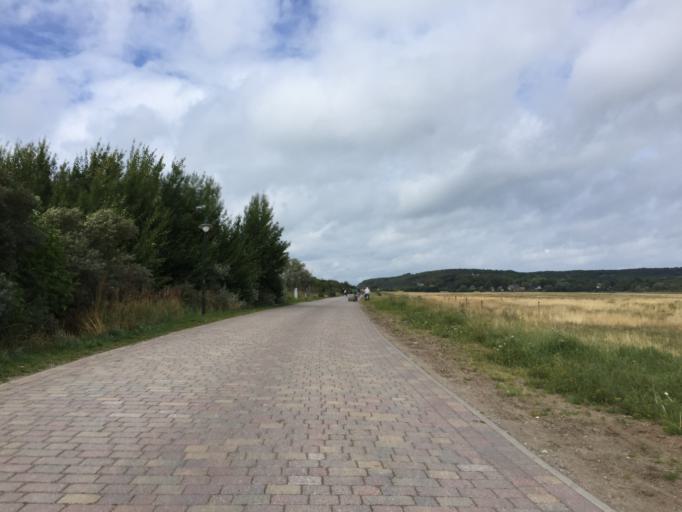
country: DE
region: Mecklenburg-Vorpommern
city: Hiddensee
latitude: 54.5751
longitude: 13.1049
